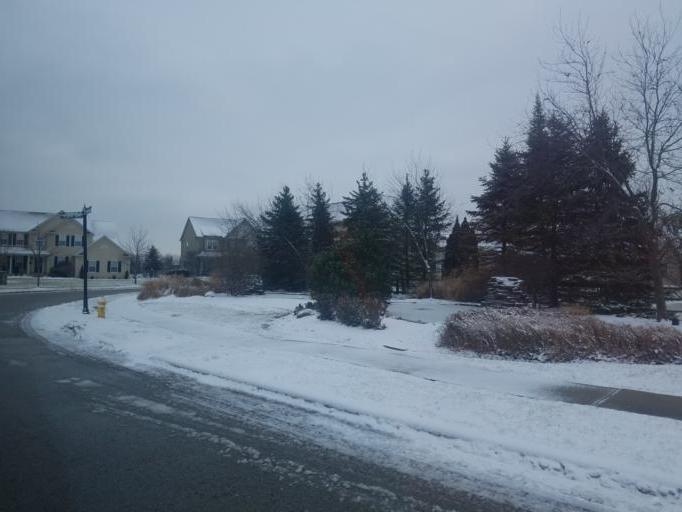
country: US
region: Ohio
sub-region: Franklin County
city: New Albany
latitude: 40.0189
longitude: -82.7978
